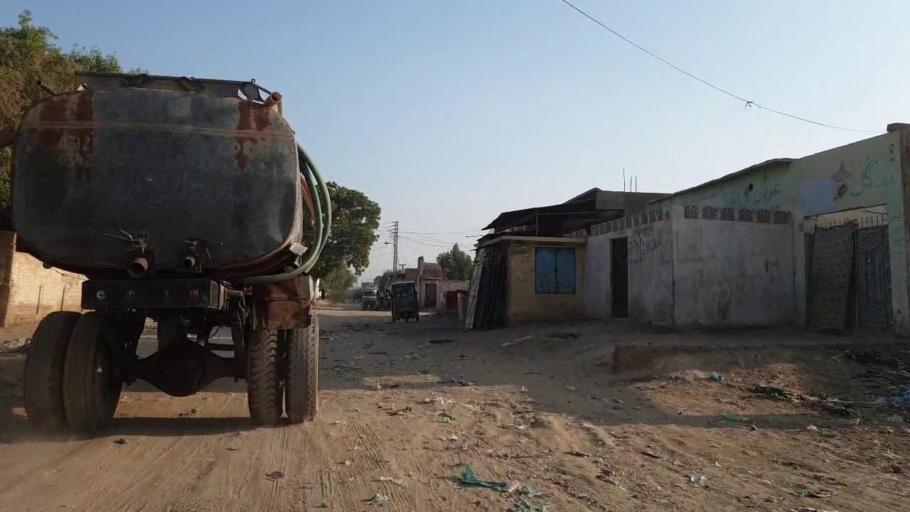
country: PK
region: Sindh
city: Kotri
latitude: 25.3587
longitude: 68.2594
